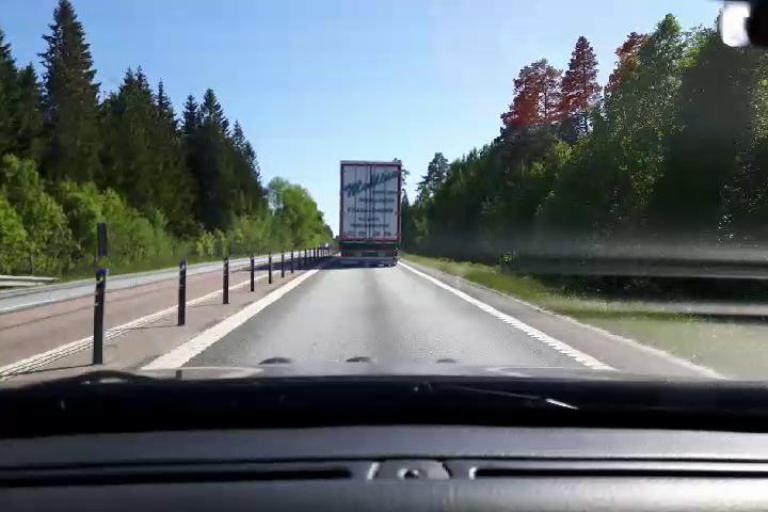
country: SE
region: Gaevleborg
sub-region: Soderhamns Kommun
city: Soderhamn
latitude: 61.2540
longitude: 17.0346
